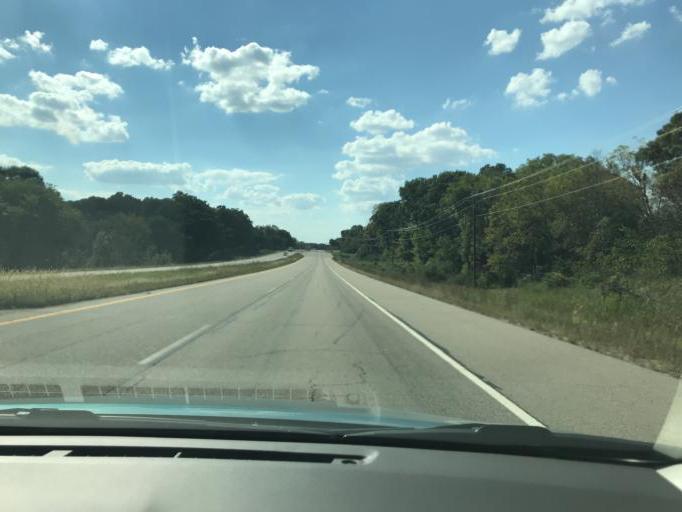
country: US
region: Wisconsin
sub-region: Walworth County
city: Como
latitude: 42.5855
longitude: -88.4877
